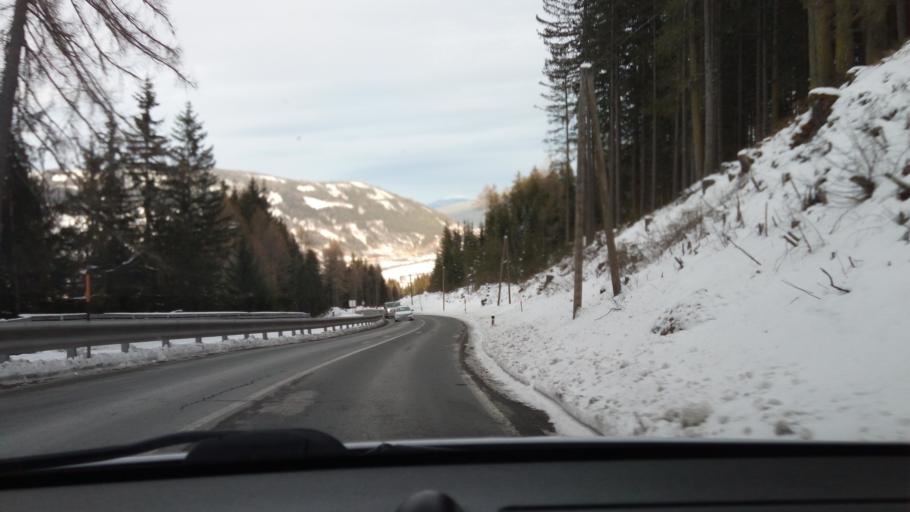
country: AT
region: Salzburg
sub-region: Politischer Bezirk Tamsweg
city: Sankt Michael im Lungau
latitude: 47.0840
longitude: 13.6194
